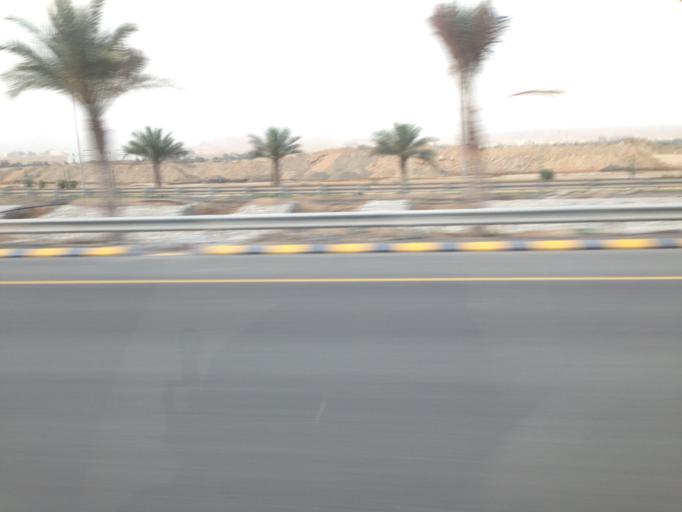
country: OM
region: Muhafazat Masqat
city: Bawshar
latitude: 23.6016
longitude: 58.3249
